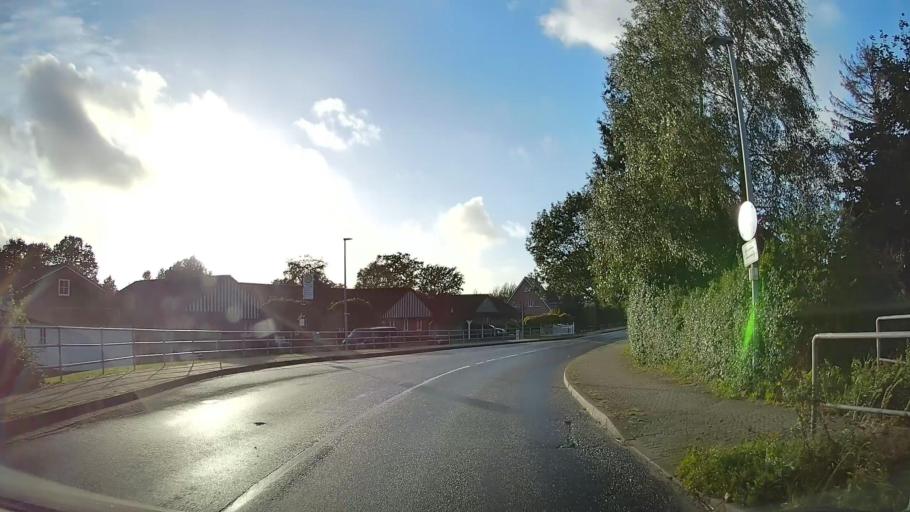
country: DE
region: Schleswig-Holstein
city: Horst
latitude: 53.8056
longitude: 9.6446
